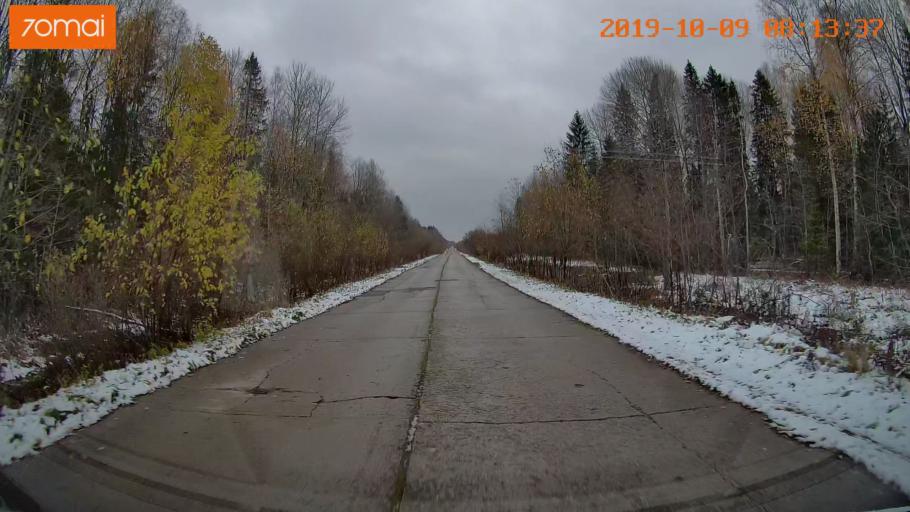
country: RU
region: Vologda
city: Gryazovets
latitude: 58.7244
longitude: 40.1428
